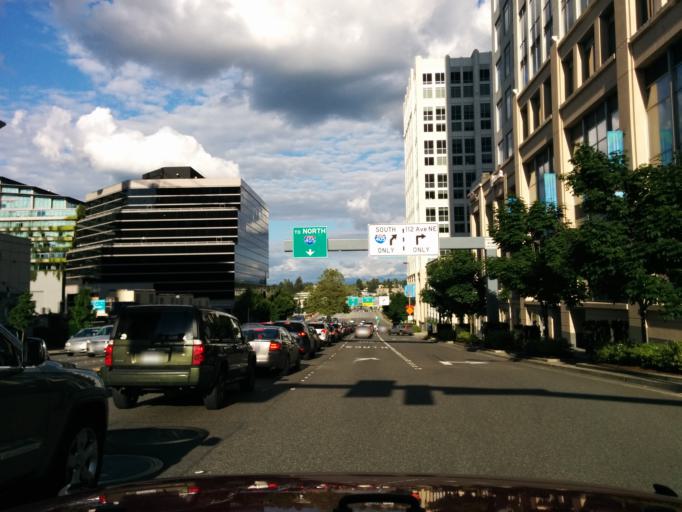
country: US
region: Washington
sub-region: King County
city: Bellevue
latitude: 47.6173
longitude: -122.1935
